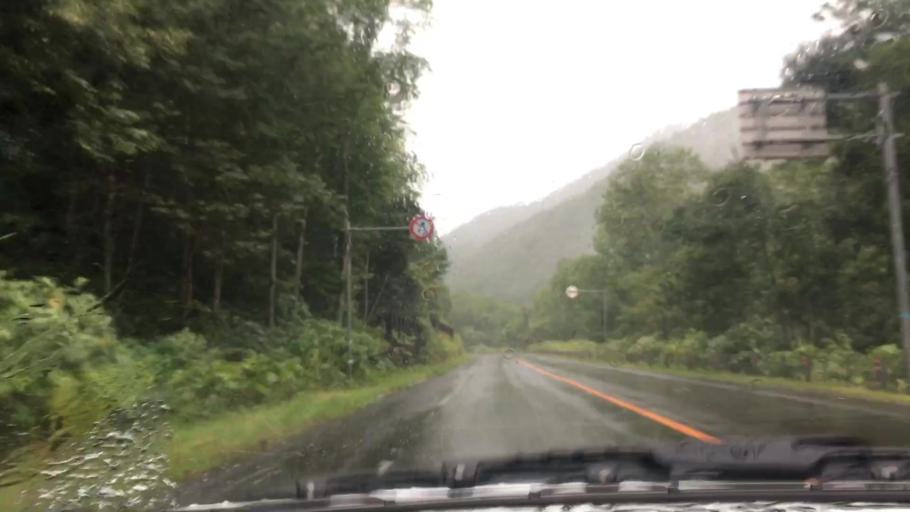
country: JP
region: Hokkaido
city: Sapporo
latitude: 42.9464
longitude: 141.1392
